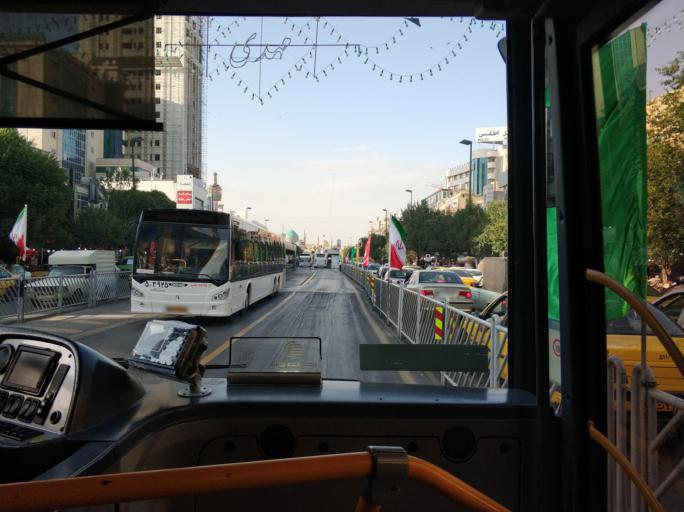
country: IR
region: Razavi Khorasan
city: Mashhad
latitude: 36.2821
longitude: 59.6107
